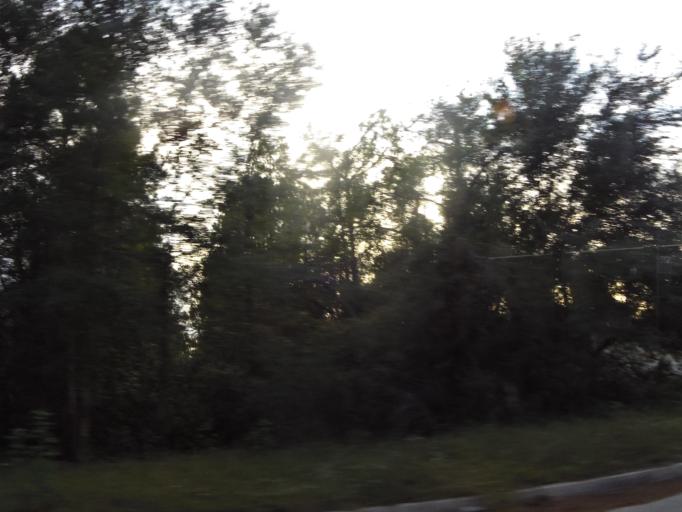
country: US
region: Florida
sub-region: Saint Johns County
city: Fruit Cove
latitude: 30.1556
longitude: -81.5390
